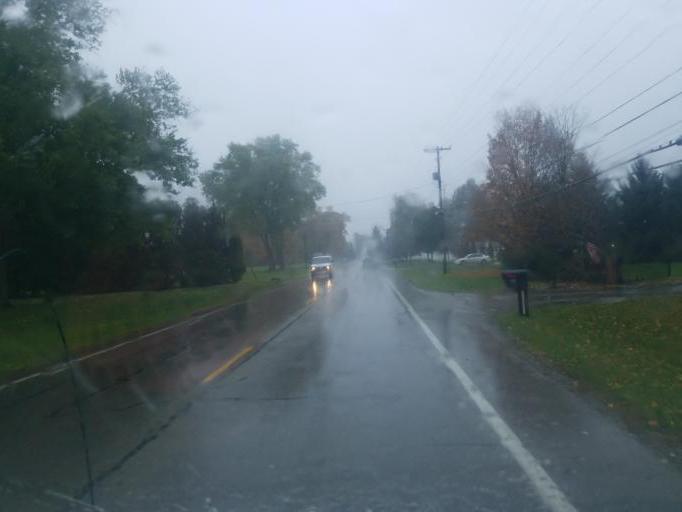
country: US
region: Ohio
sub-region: Muskingum County
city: Zanesville
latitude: 39.9630
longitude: -82.0416
